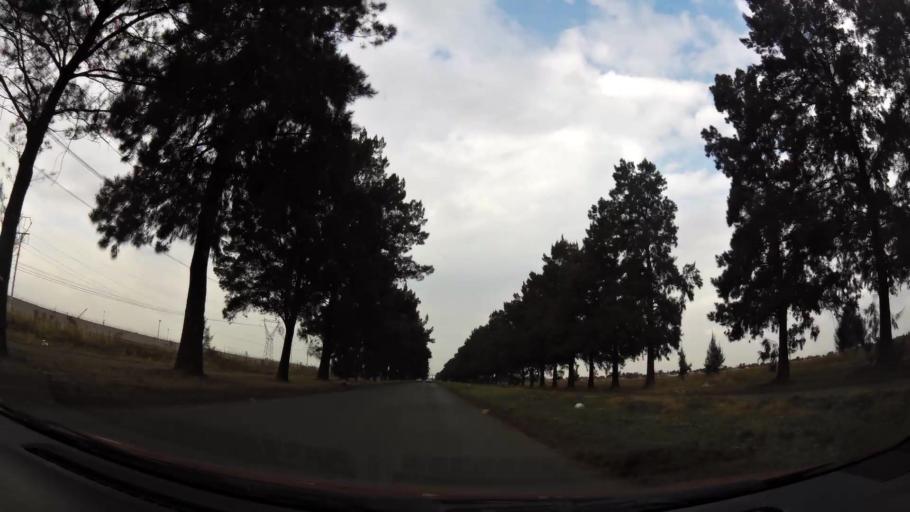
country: ZA
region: Gauteng
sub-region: Sedibeng District Municipality
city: Vanderbijlpark
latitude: -26.6740
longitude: 27.8238
